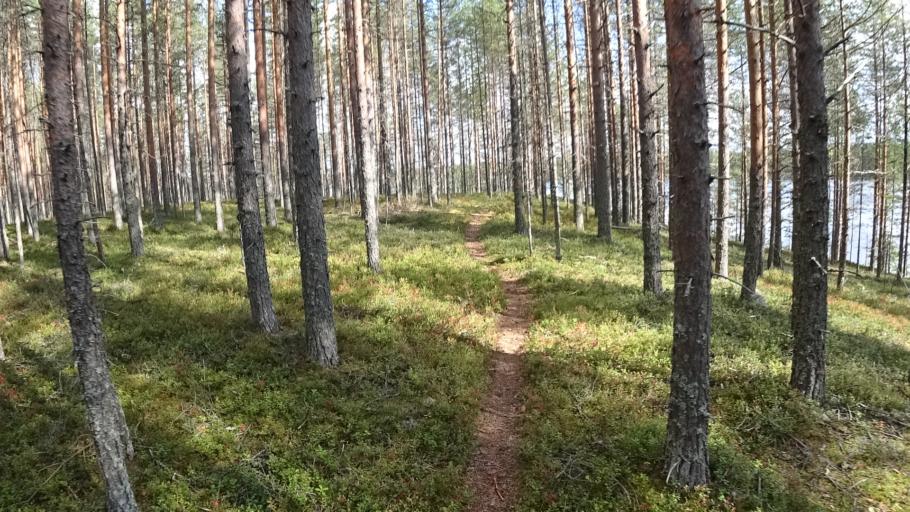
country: FI
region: North Karelia
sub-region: Joensuu
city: Ilomantsi
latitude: 62.6061
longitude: 31.1885
